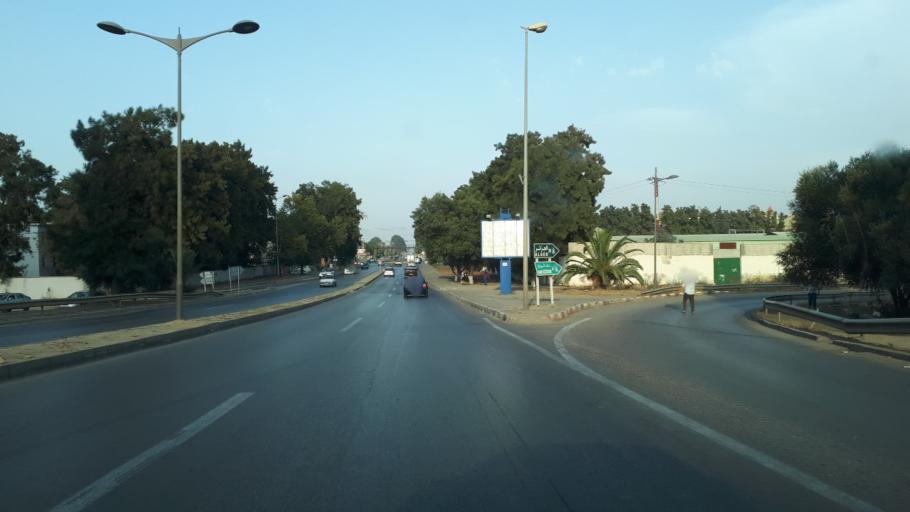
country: DZ
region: Alger
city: Dar el Beida
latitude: 36.7276
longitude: 3.2134
